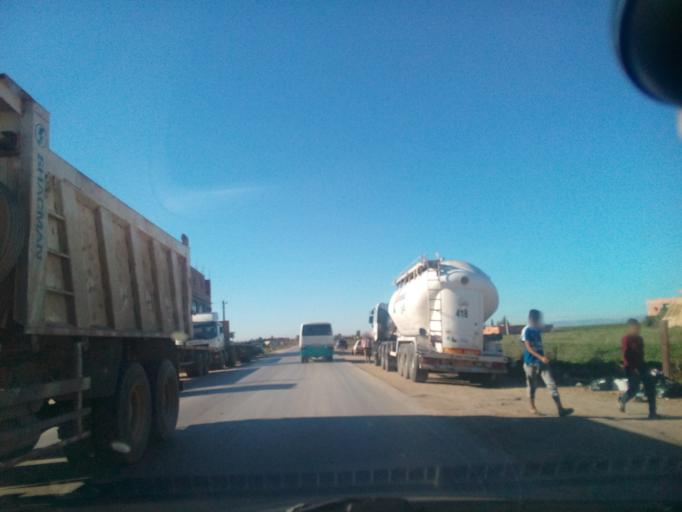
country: DZ
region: Relizane
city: Djidiouia
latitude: 35.8964
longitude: 0.6929
